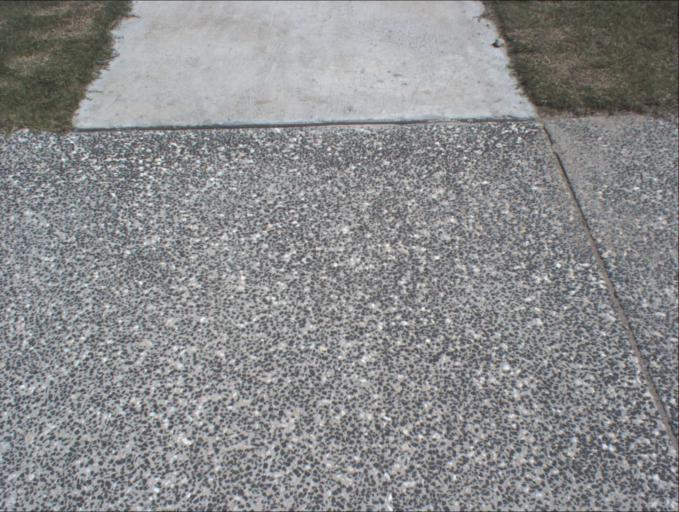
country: AU
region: Queensland
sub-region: Logan
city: Beenleigh
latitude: -27.7164
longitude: 153.1666
